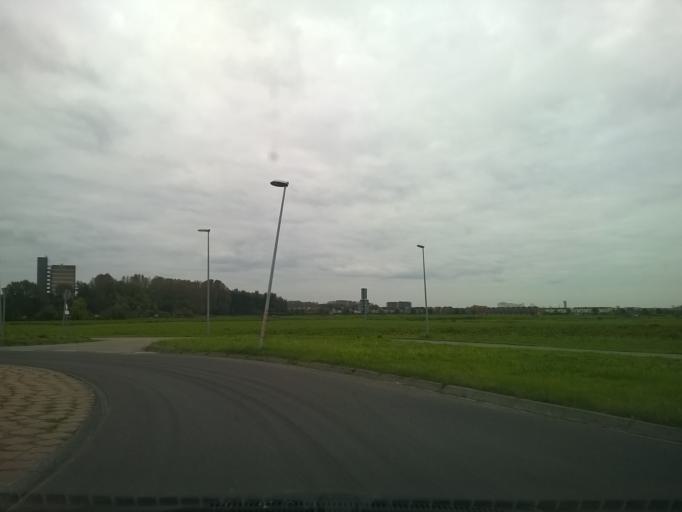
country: NL
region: Groningen
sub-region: Gemeente Groningen
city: Korrewegwijk
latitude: 53.2356
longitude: 6.5195
